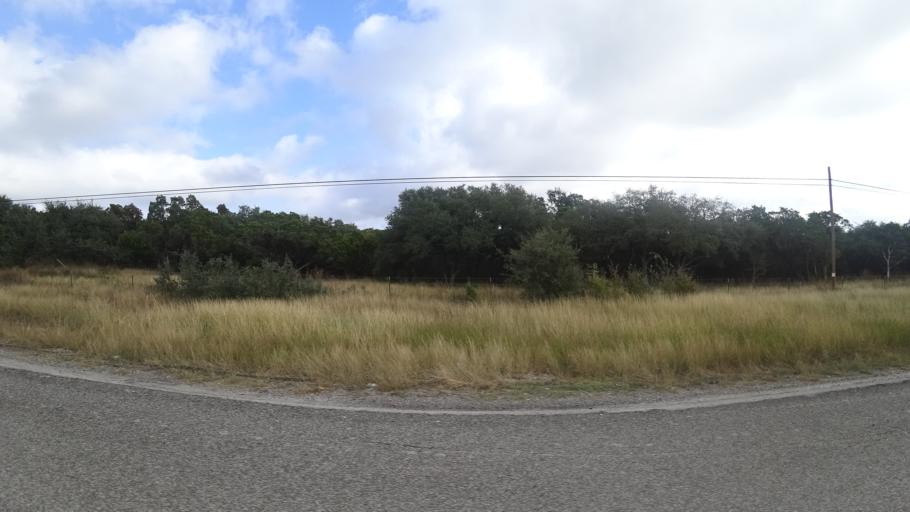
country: US
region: Texas
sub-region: Travis County
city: Bee Cave
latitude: 30.2984
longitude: -97.9276
